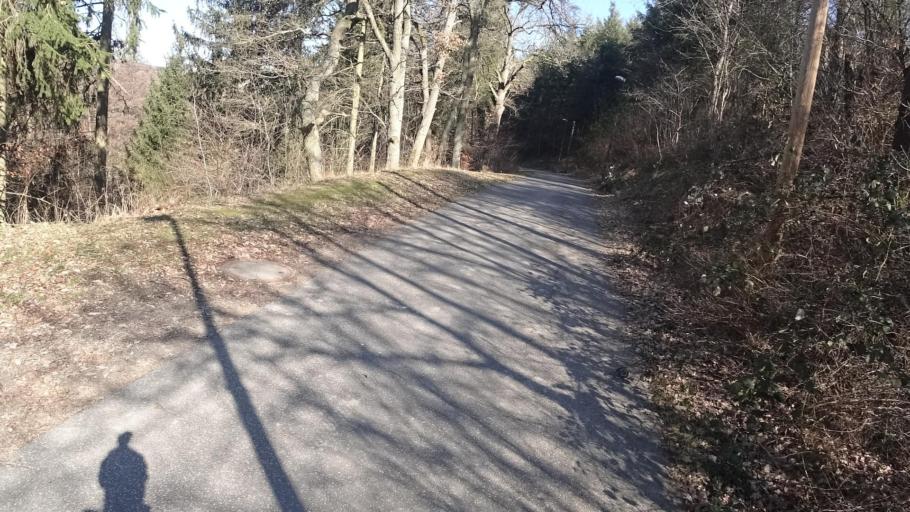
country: DE
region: Rheinland-Pfalz
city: Simmern
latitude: 49.9921
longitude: 7.5361
